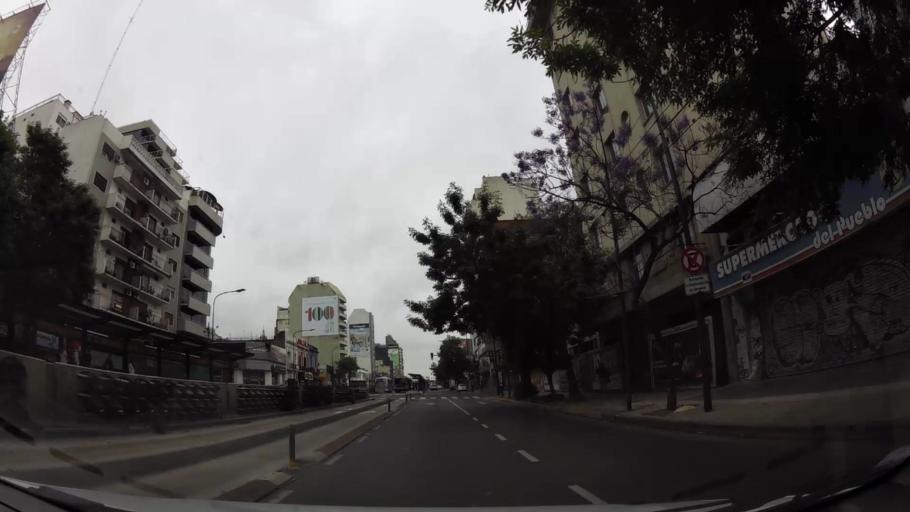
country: AR
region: Buenos Aires F.D.
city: Colegiales
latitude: -34.5441
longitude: -58.4718
